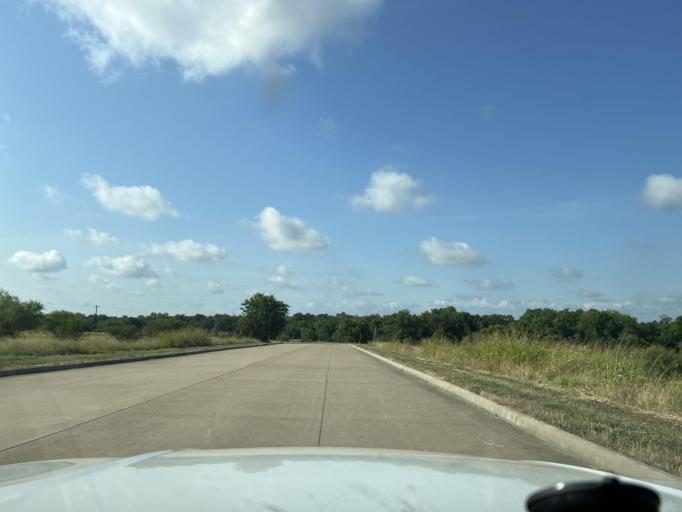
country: US
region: Texas
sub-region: Washington County
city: Brenham
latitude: 30.1375
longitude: -96.3806
